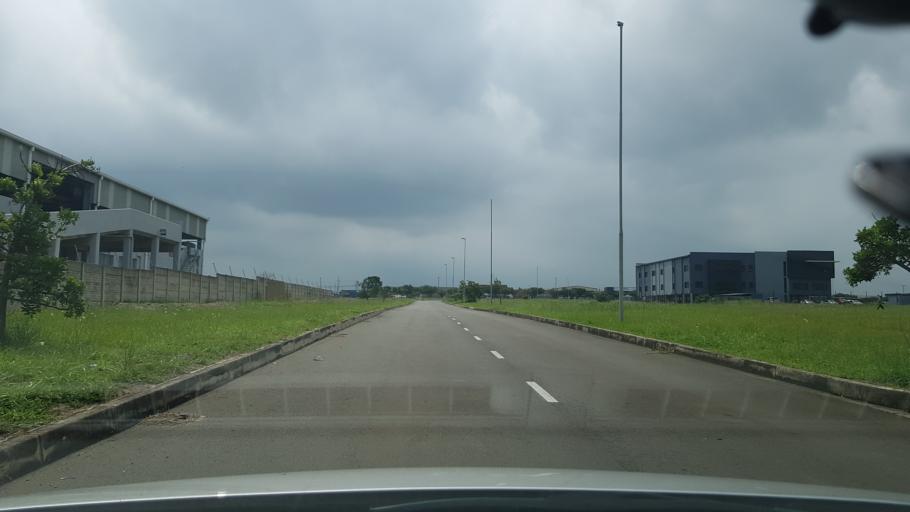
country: ZA
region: KwaZulu-Natal
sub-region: uThungulu District Municipality
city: Richards Bay
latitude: -28.7577
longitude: 32.0485
